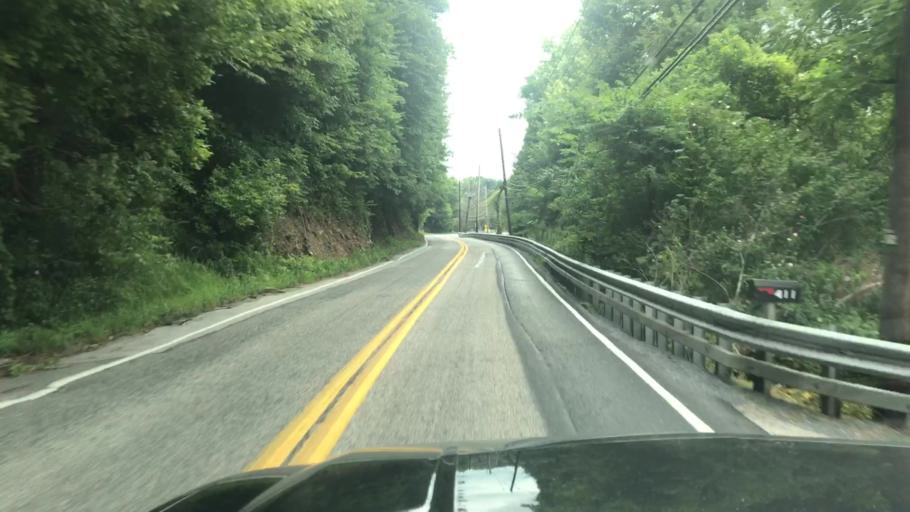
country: US
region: Pennsylvania
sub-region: Cumberland County
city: Shiremanstown
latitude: 40.2454
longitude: -76.9715
